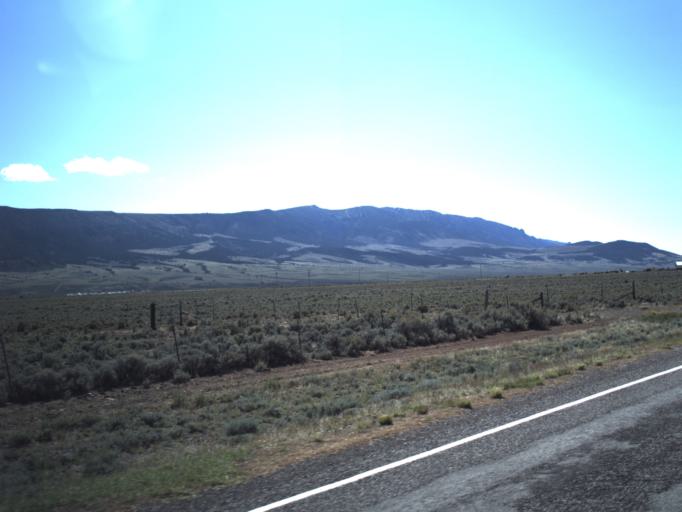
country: US
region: Utah
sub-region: Sevier County
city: Monroe
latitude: 38.4381
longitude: -111.9201
